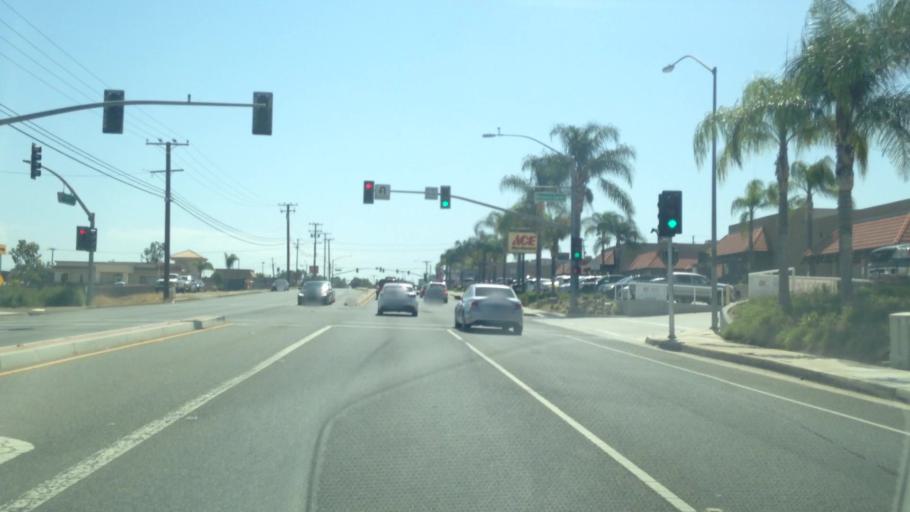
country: US
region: California
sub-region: Riverside County
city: Woodcrest
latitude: 33.8872
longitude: -117.3346
